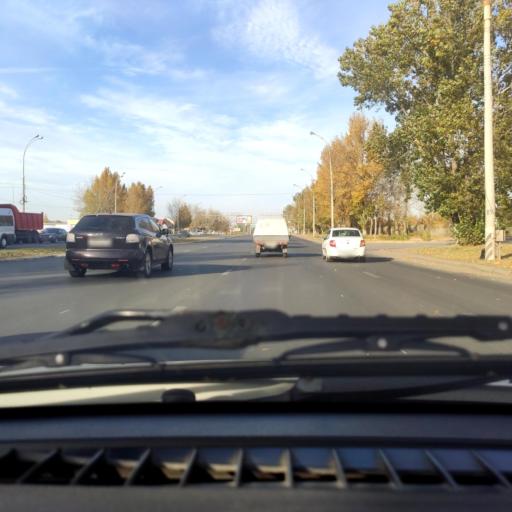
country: RU
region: Samara
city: Tol'yatti
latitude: 53.5387
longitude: 49.2843
